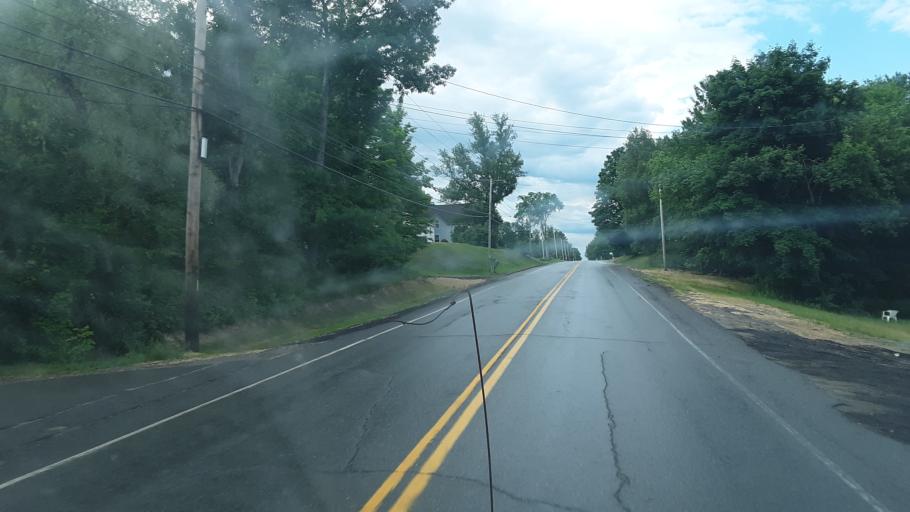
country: US
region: Maine
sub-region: Penobscot County
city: Lincoln
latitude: 45.3871
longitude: -68.4966
